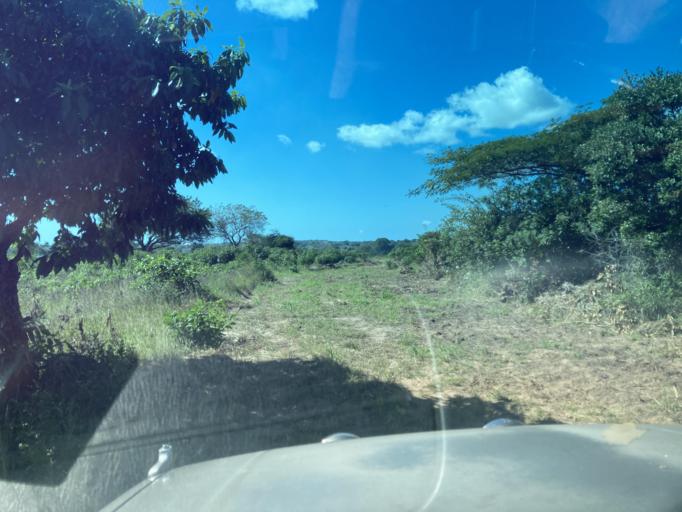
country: MZ
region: Maputo City
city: Maputo
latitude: -26.0506
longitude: 32.5501
